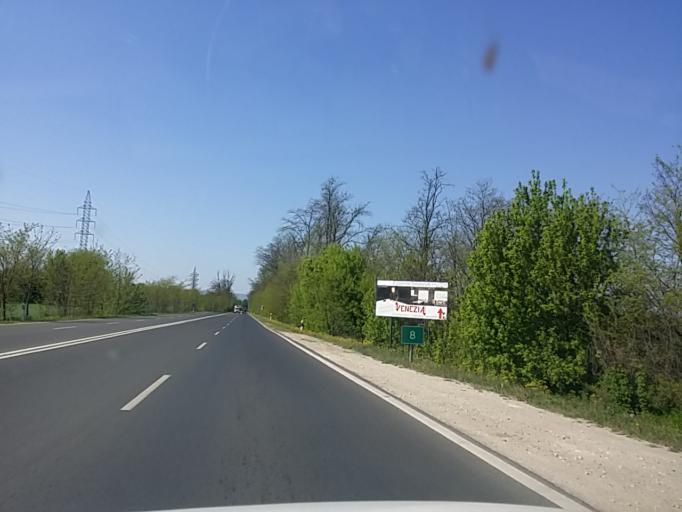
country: HU
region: Pest
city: Fot
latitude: 47.5889
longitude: 19.1633
